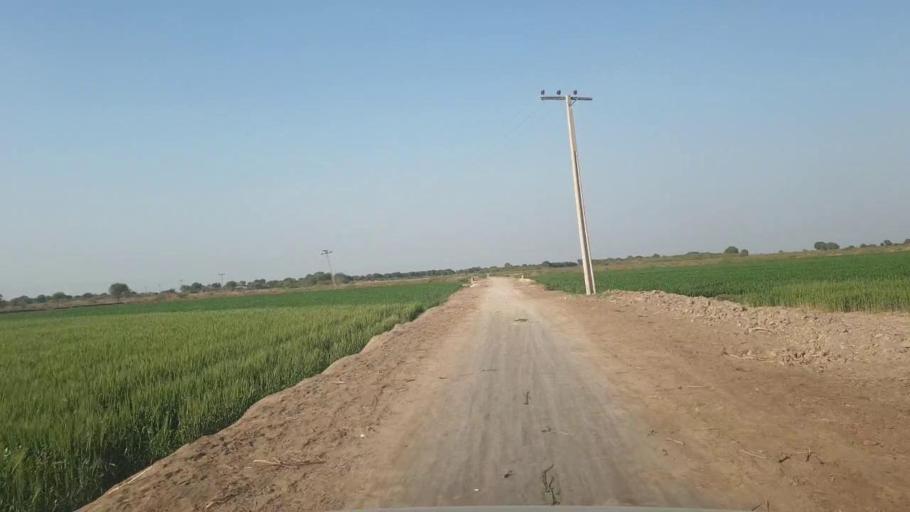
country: PK
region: Sindh
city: Chambar
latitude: 25.2970
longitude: 68.8630
